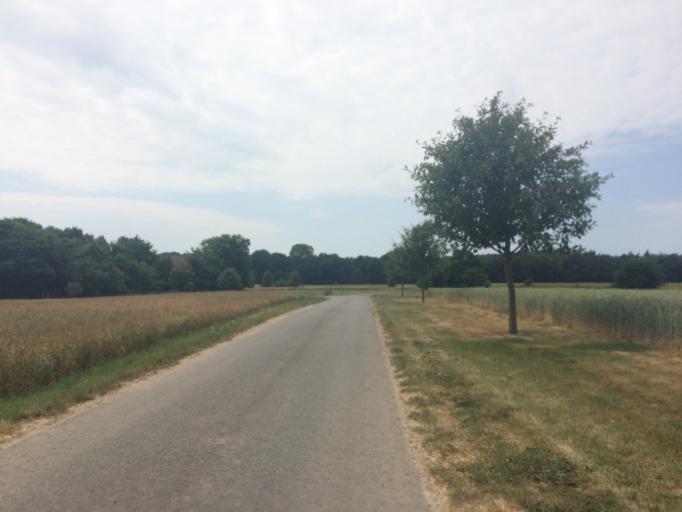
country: DK
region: Capital Region
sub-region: Bornholm Kommune
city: Ronne
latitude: 55.1748
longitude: 14.7261
